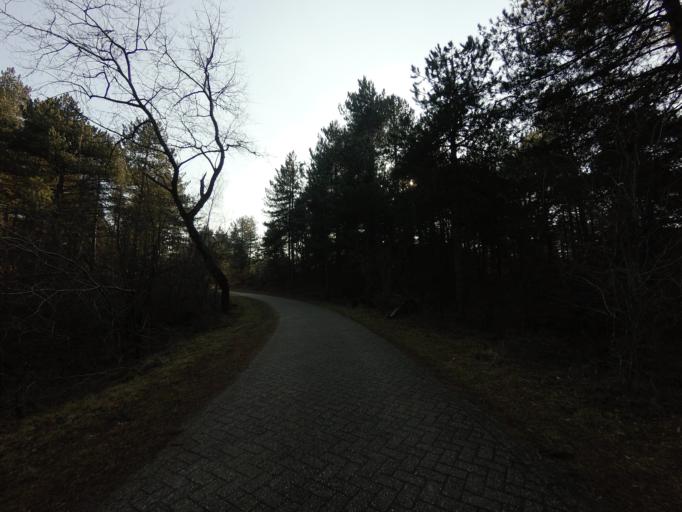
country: NL
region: North Holland
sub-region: Gemeente Bloemendaal
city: Bloemendaal
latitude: 52.4142
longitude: 4.6045
